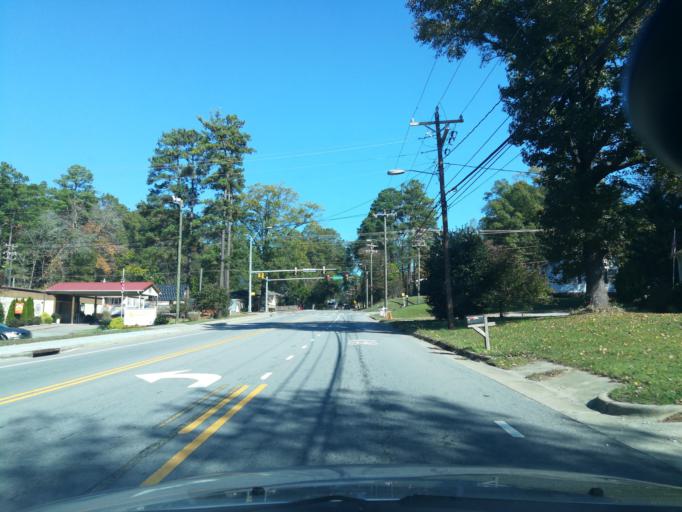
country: US
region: North Carolina
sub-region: Durham County
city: Durham
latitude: 36.0348
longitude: -78.9098
